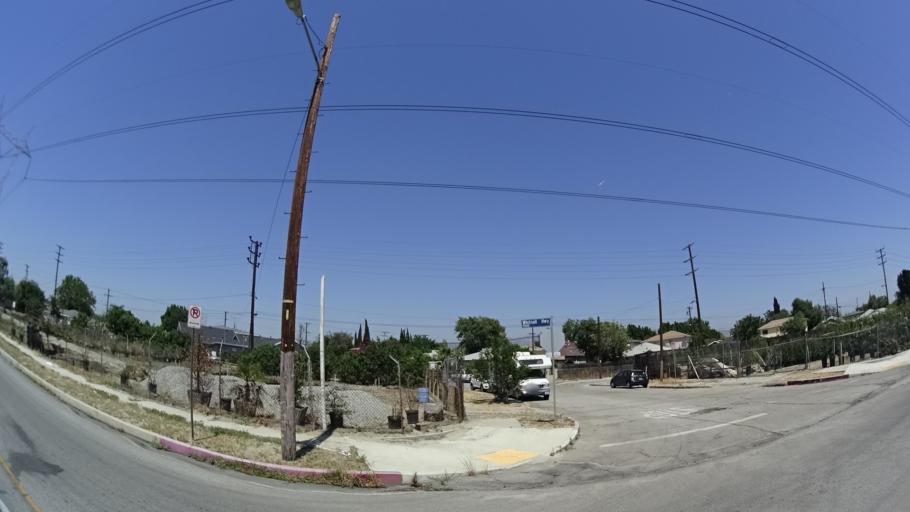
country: US
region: California
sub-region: Los Angeles County
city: North Hollywood
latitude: 34.1782
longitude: -118.3644
